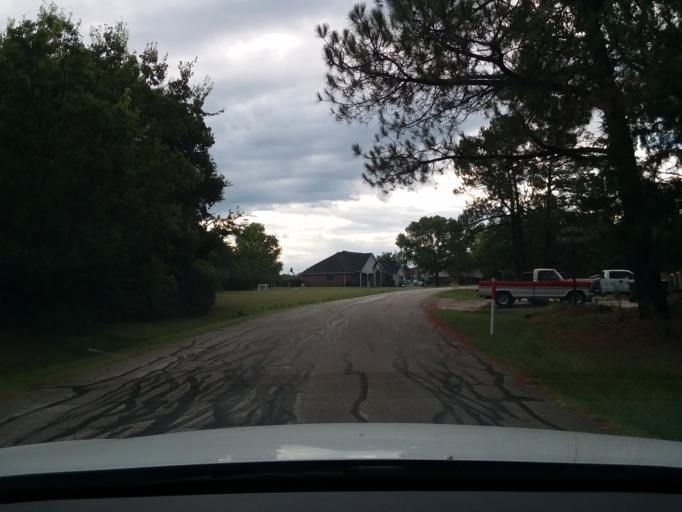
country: US
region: Texas
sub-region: Denton County
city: Double Oak
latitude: 33.0680
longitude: -97.0991
